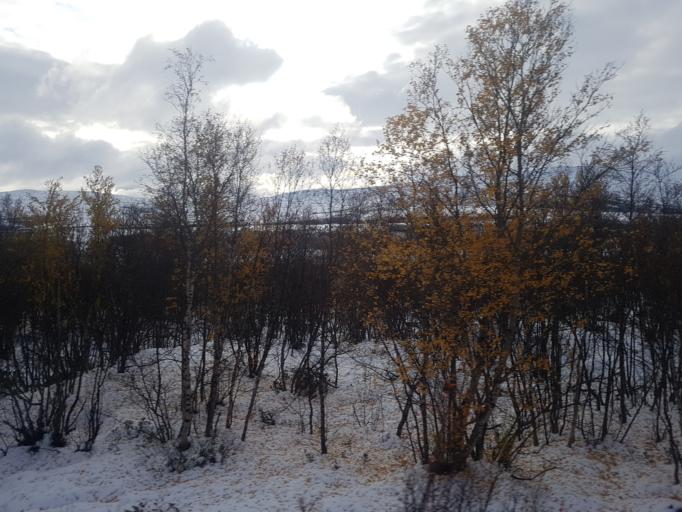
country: NO
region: Oppland
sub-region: Dovre
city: Dovre
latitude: 62.1950
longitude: 9.5185
